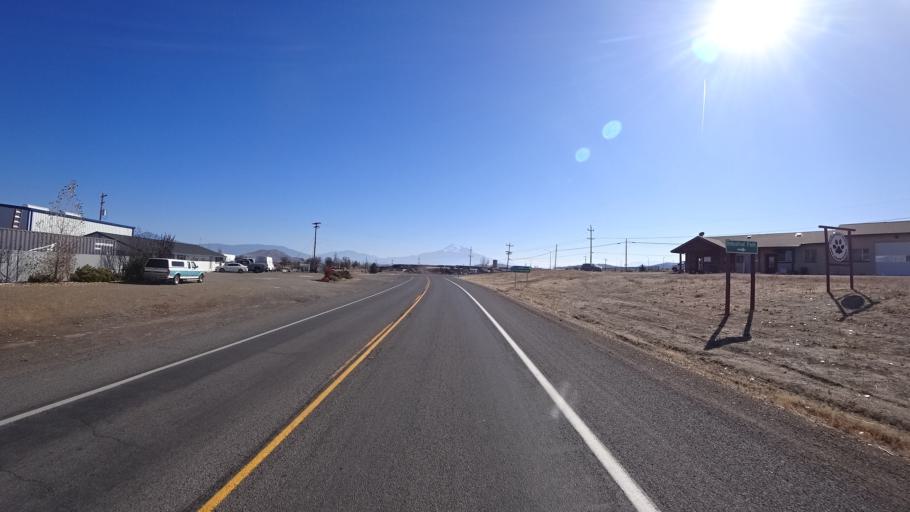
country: US
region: California
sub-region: Siskiyou County
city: Yreka
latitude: 41.7361
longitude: -122.5943
